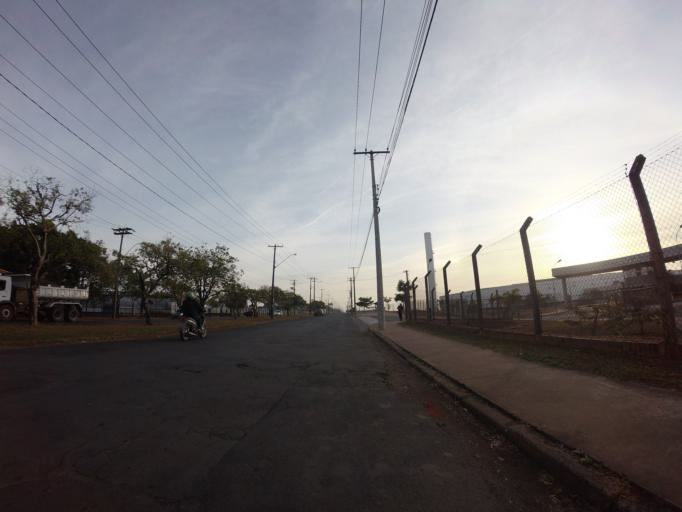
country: BR
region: Sao Paulo
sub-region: Piracicaba
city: Piracicaba
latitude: -22.7354
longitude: -47.5889
